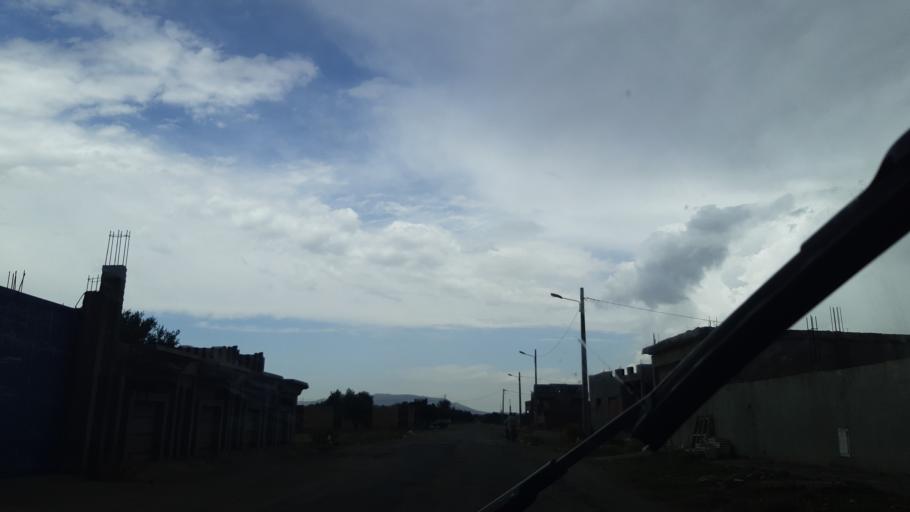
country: TN
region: Al Qayrawan
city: Sbikha
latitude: 36.1243
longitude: 10.0873
